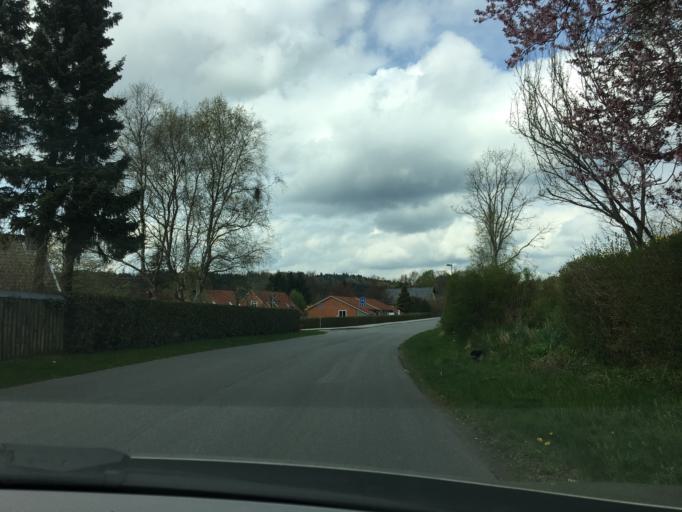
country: DK
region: Central Jutland
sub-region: Skanderborg Kommune
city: Ry
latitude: 56.0699
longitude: 9.6996
